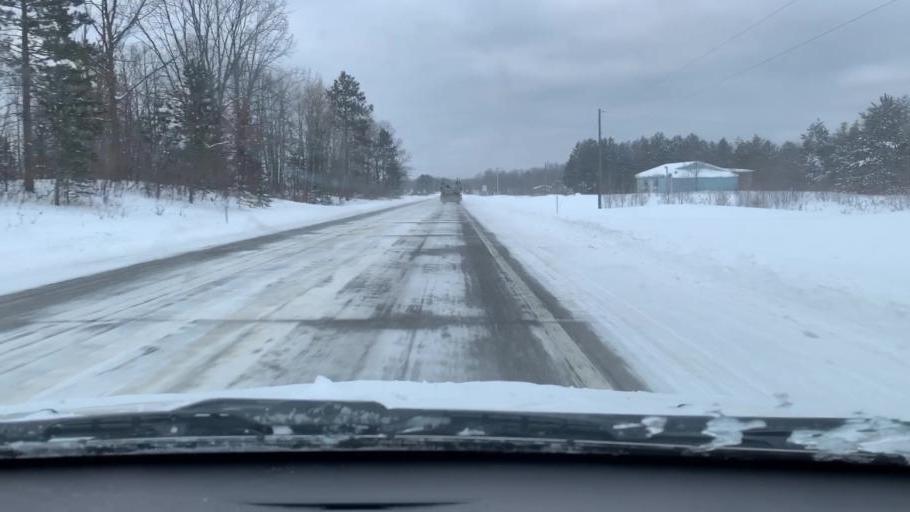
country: US
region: Michigan
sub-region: Wexford County
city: Manton
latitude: 44.6005
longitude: -85.3283
